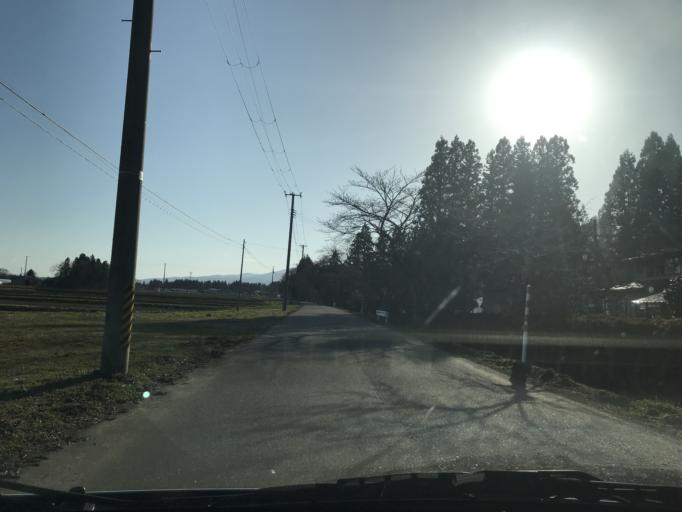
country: JP
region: Iwate
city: Kitakami
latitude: 39.2600
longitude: 141.0434
